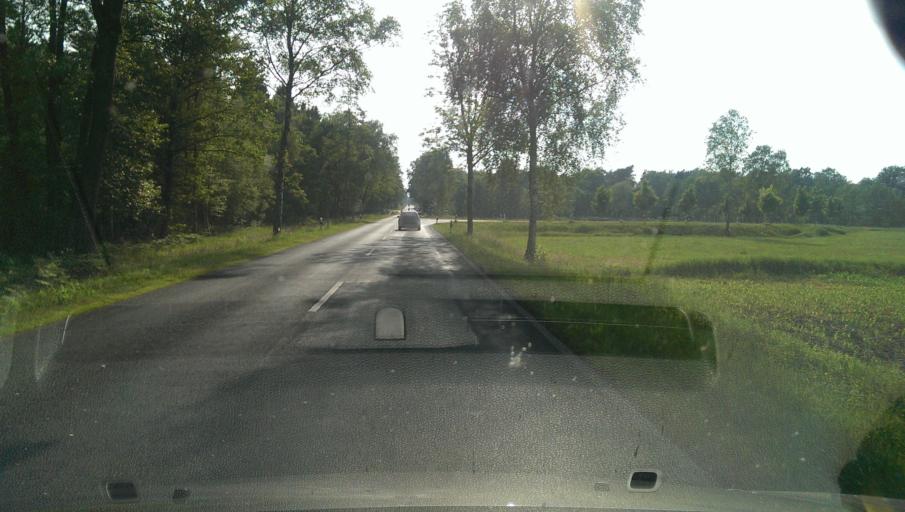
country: DE
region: Lower Saxony
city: Wietzendorf
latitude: 52.9345
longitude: 9.9862
